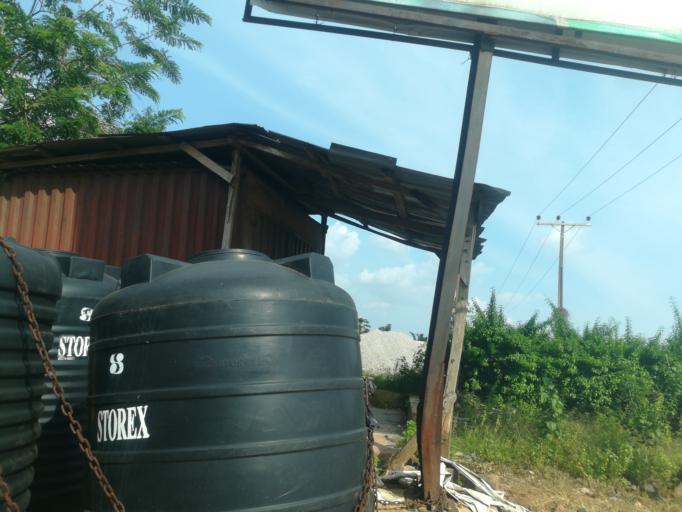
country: NG
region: Oyo
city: Ido
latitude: 7.3991
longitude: 3.8053
